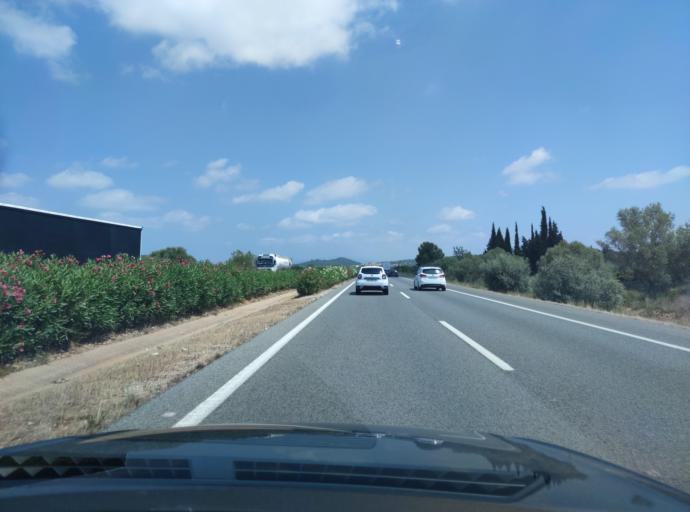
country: ES
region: Catalonia
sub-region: Provincia de Tarragona
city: Santa Barbara
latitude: 40.6460
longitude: 0.5051
